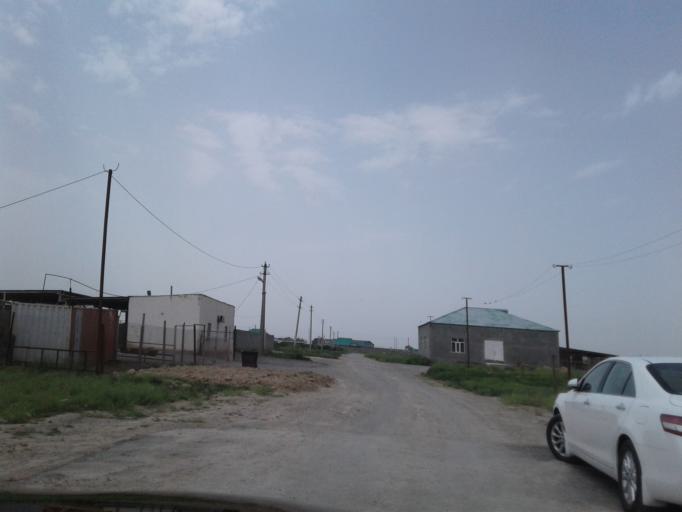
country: TM
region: Ahal
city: Ashgabat
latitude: 37.9818
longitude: 58.3181
